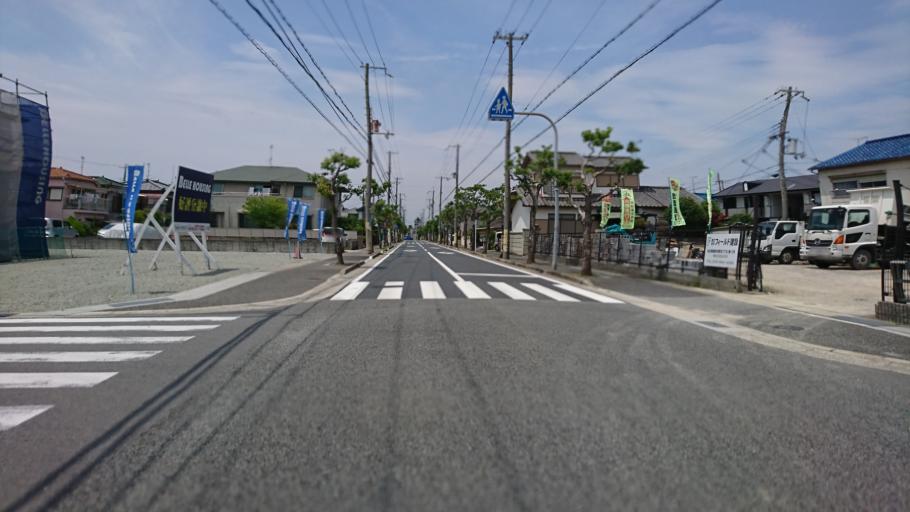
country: JP
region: Hyogo
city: Kakogawacho-honmachi
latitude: 34.7208
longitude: 134.8808
